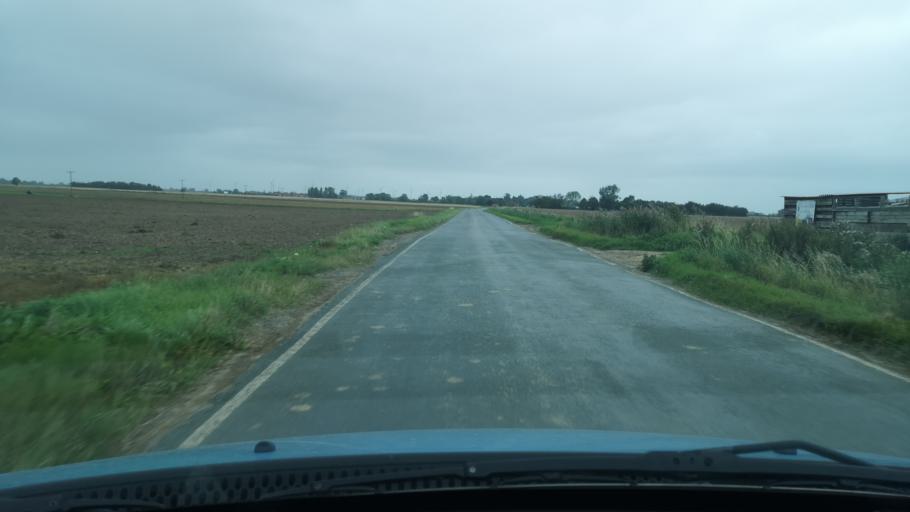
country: GB
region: England
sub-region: East Riding of Yorkshire
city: Laxton
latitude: 53.6974
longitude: -0.8125
